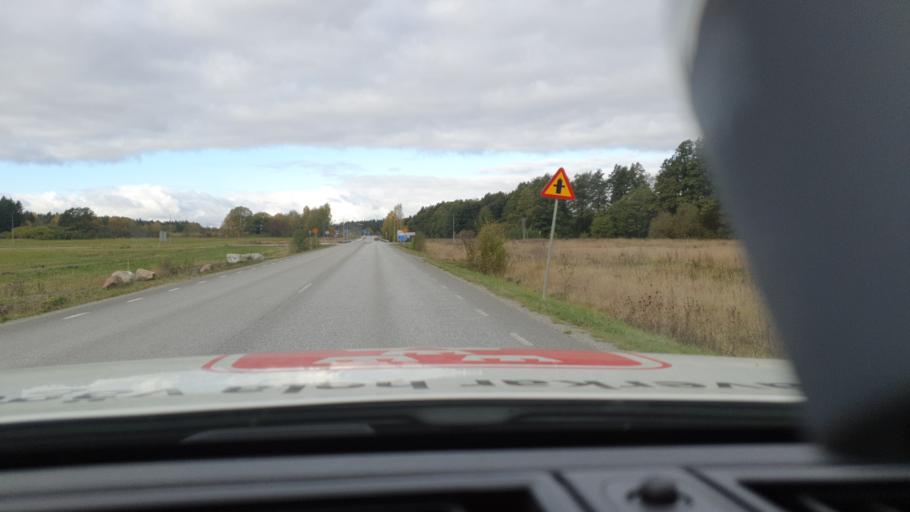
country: SE
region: Stockholm
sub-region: Upplands-Bro Kommun
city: Bro
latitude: 59.5089
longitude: 17.6323
